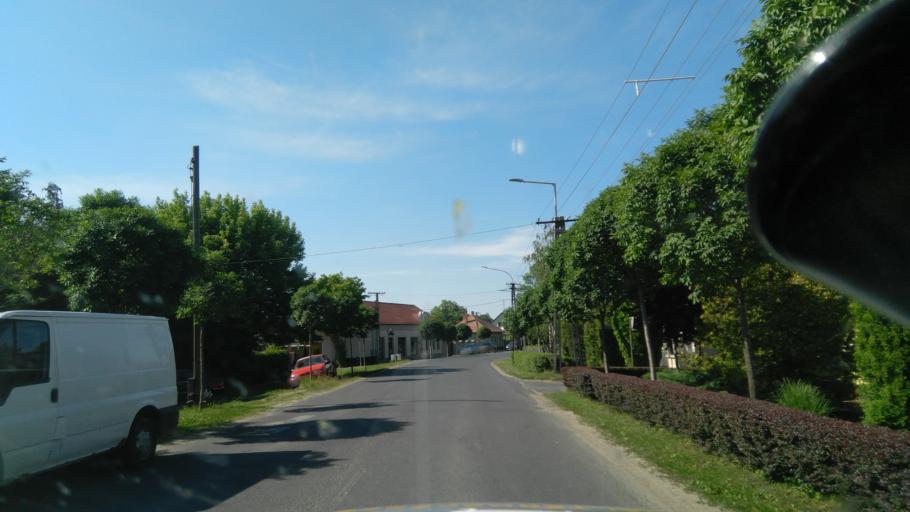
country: HU
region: Bekes
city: Gyula
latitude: 46.6488
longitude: 21.2838
